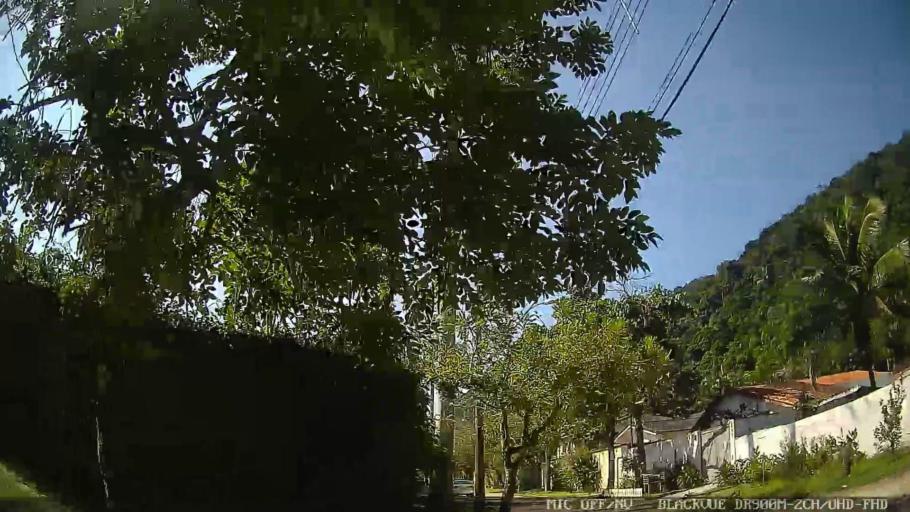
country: BR
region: Sao Paulo
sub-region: Guaruja
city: Guaruja
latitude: -24.0167
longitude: -46.2852
